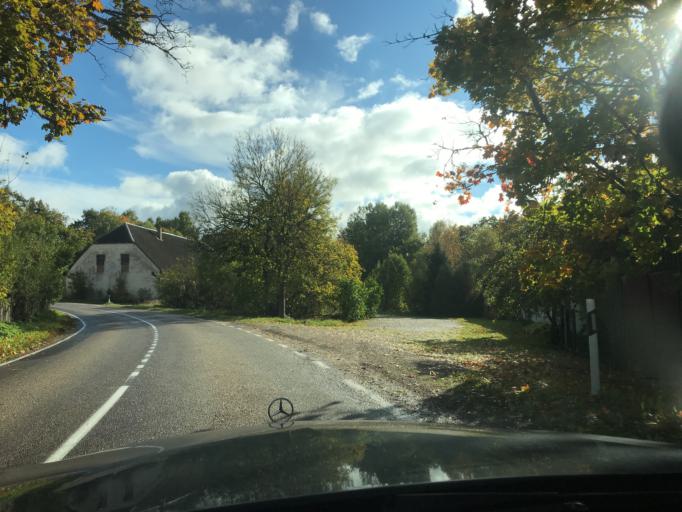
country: EE
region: Valgamaa
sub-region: Torva linn
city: Torva
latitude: 58.0089
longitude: 26.2021
